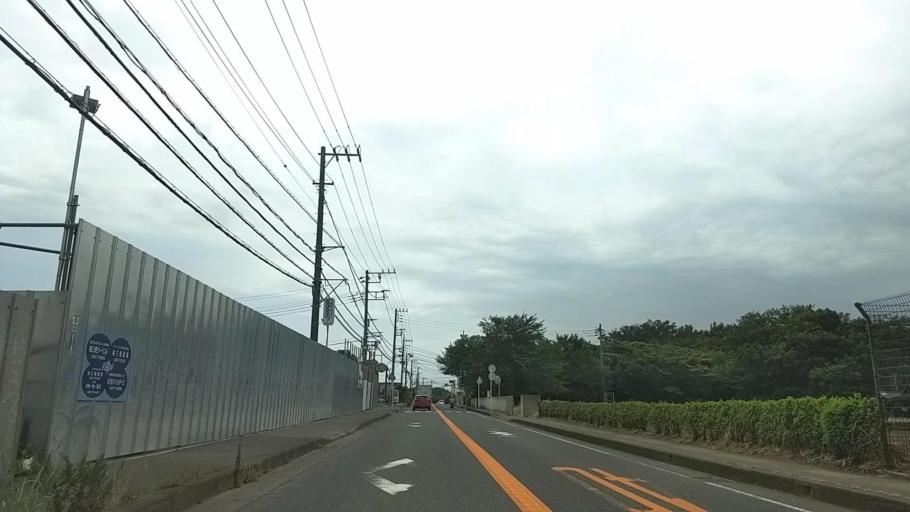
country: JP
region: Kanagawa
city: Chigasaki
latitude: 35.3689
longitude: 139.4180
